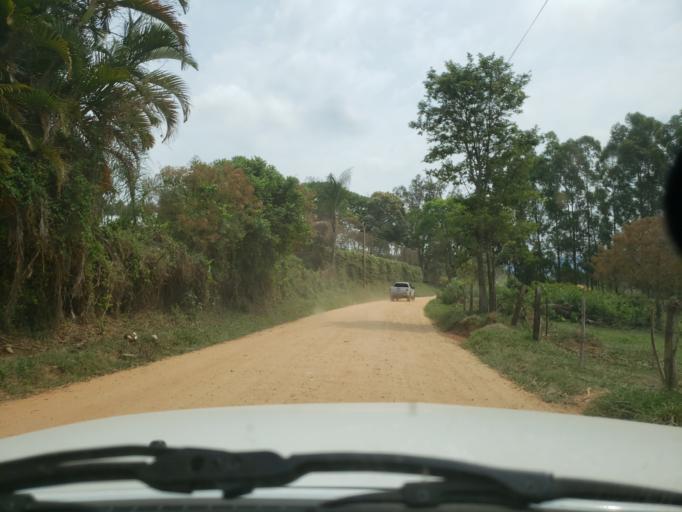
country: BR
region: Minas Gerais
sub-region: Jacutinga
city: Jacutinga
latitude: -22.3083
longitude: -46.6067
